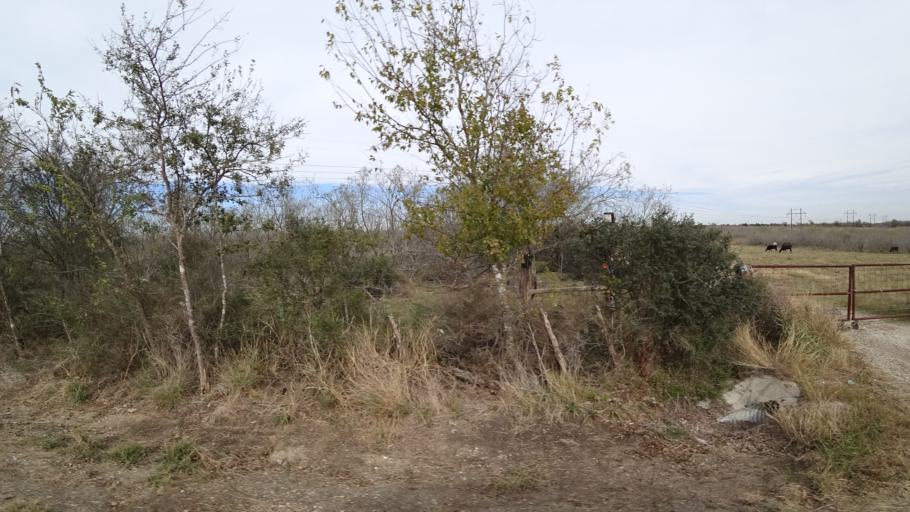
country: US
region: Texas
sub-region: Travis County
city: Garfield
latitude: 30.1408
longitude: -97.6138
